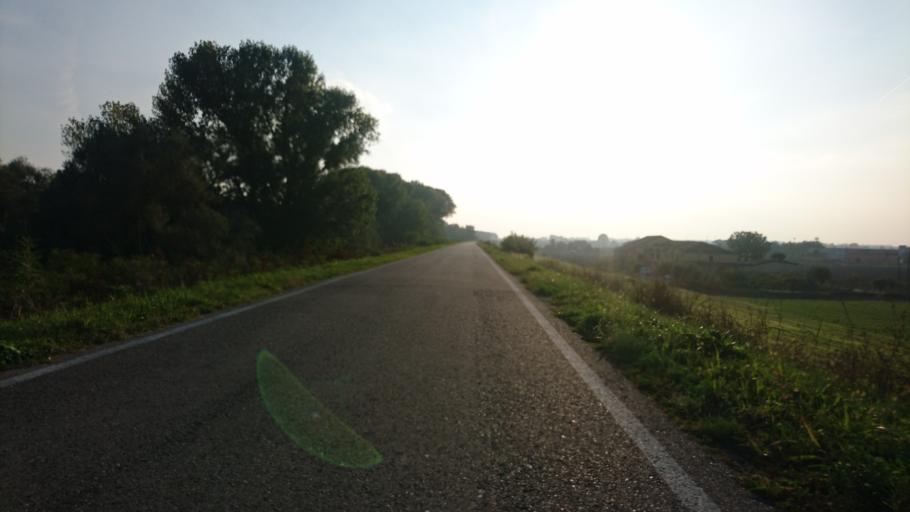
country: IT
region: Emilia-Romagna
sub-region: Provincia di Ferrara
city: Francolino
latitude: 44.9009
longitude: 11.6419
